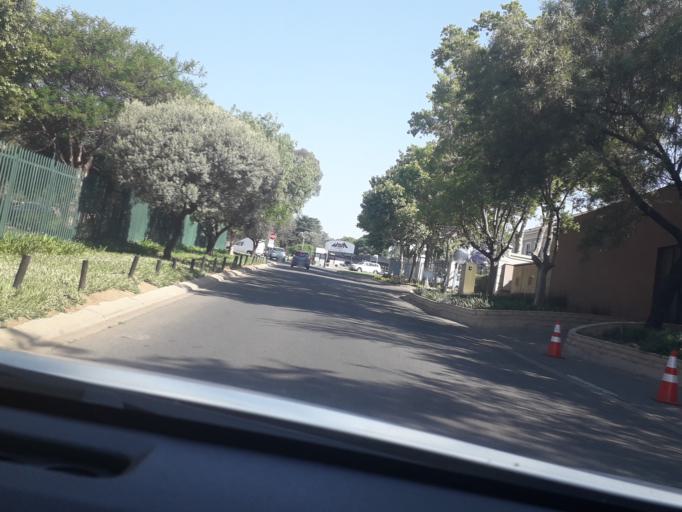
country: ZA
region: Gauteng
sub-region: City of Johannesburg Metropolitan Municipality
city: Diepsloot
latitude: -26.0674
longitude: 28.0172
